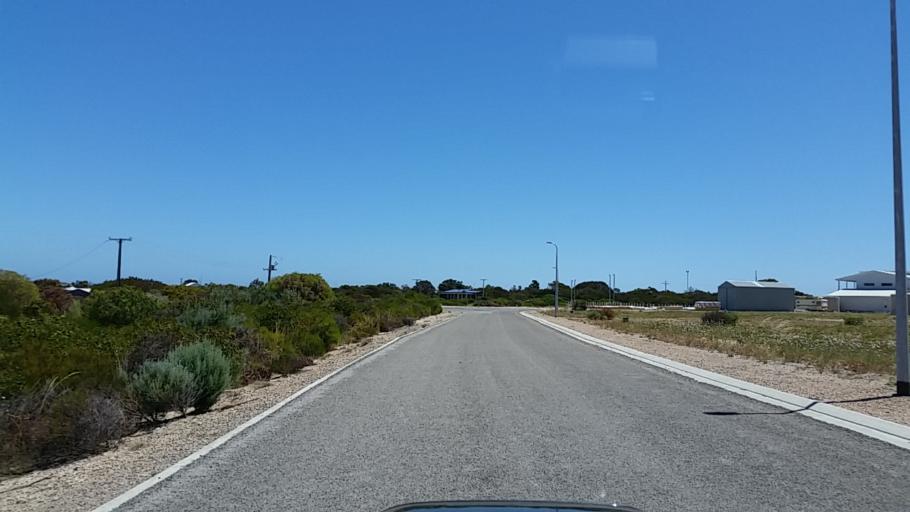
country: AU
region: South Australia
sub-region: Yorke Peninsula
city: Honiton
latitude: -35.2335
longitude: 136.9843
